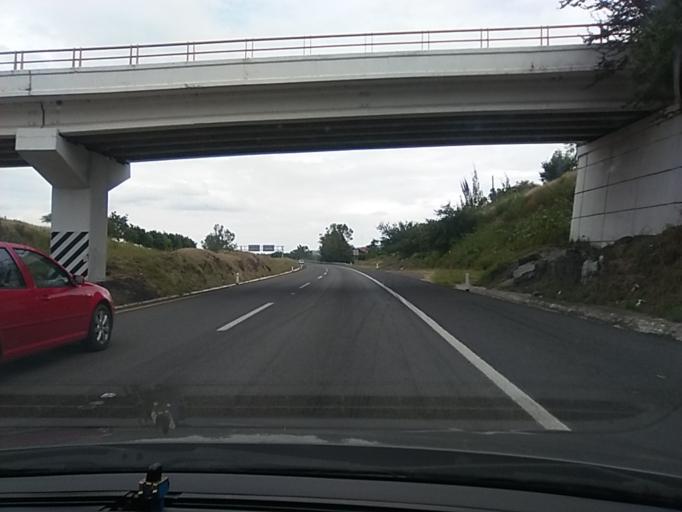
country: MX
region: Jalisco
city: Ocotlan
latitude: 20.4019
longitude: -102.7353
